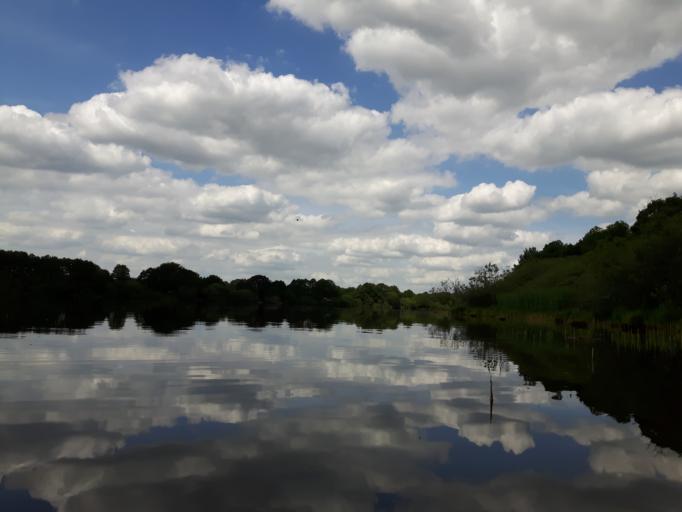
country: DE
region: Schleswig-Holstein
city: Muhbrook
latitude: 54.1496
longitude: 10.0103
